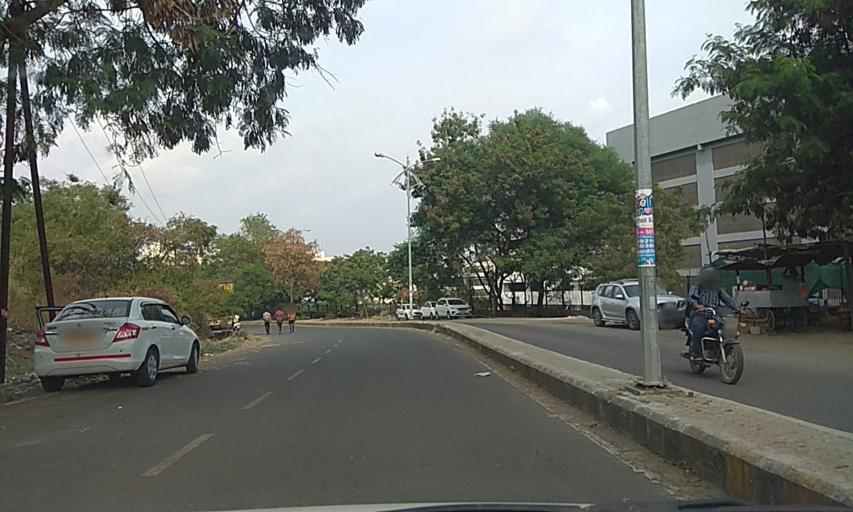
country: IN
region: Maharashtra
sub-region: Pune Division
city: Pimpri
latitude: 18.6009
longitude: 73.7153
